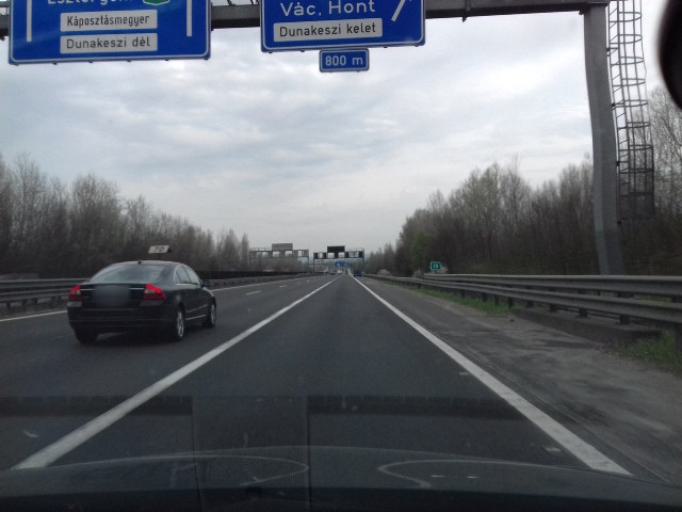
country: HU
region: Budapest
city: Budapest XV. keruelet
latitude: 47.5866
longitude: 19.1444
